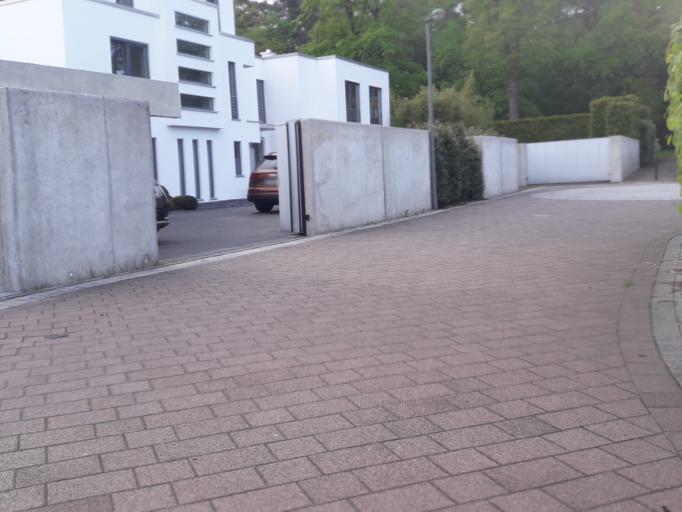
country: DE
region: North Rhine-Westphalia
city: Bad Lippspringe
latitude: 51.7853
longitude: 8.8078
